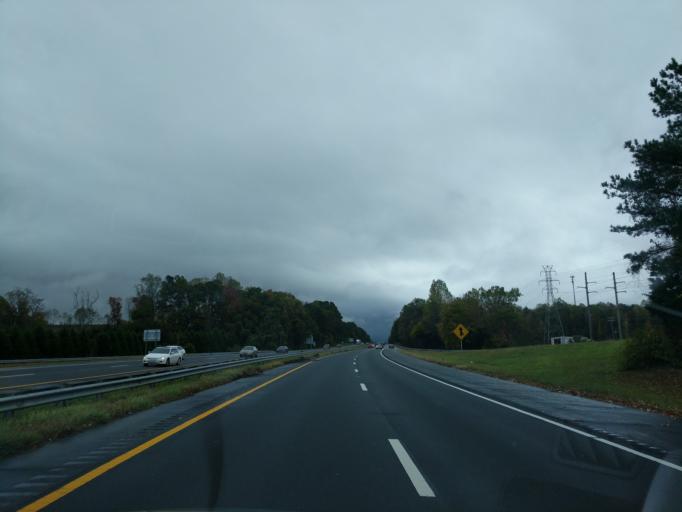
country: US
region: North Carolina
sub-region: Orange County
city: Hillsborough
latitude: 36.0587
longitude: -79.0813
